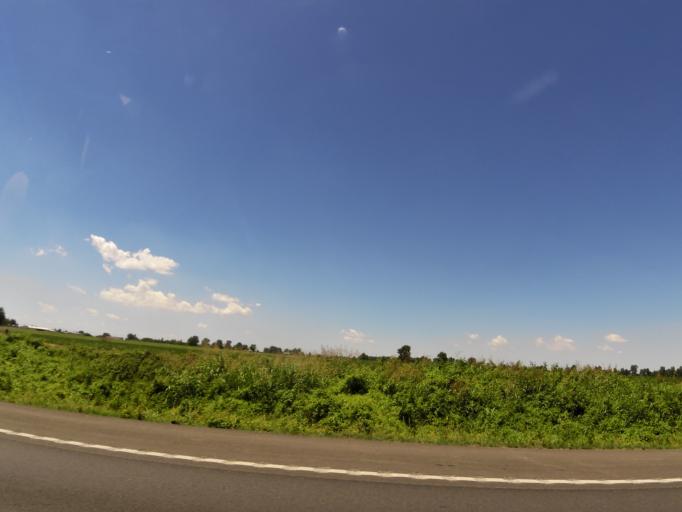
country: US
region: Missouri
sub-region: New Madrid County
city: Portageville
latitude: 36.4431
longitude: -89.6709
